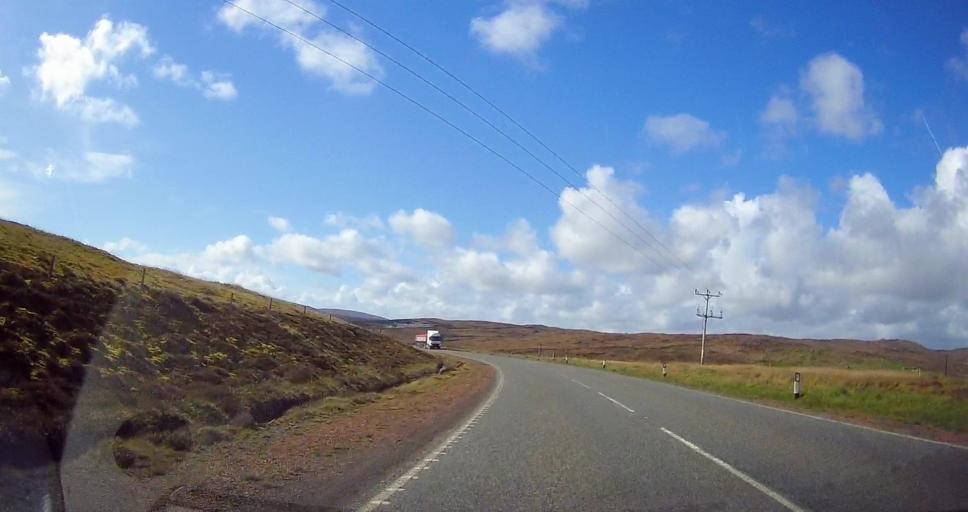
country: GB
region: Scotland
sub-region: Shetland Islands
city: Lerwick
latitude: 60.2643
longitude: -1.2222
